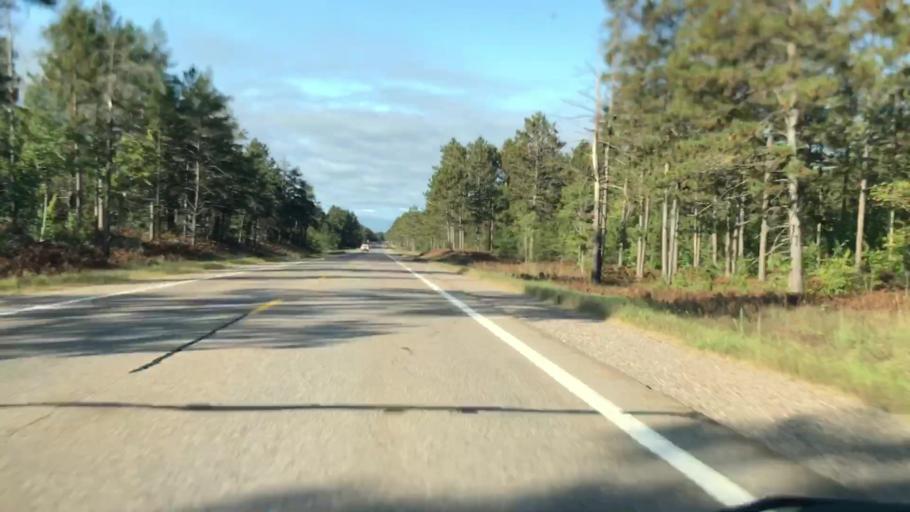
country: US
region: Michigan
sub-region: Mackinac County
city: Saint Ignace
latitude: 46.3558
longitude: -84.8954
